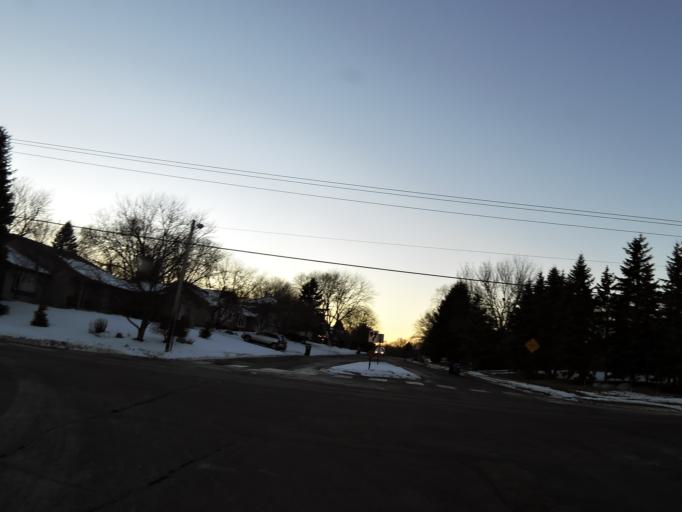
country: US
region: Minnesota
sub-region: Scott County
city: Savage
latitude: 44.8273
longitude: -93.3583
